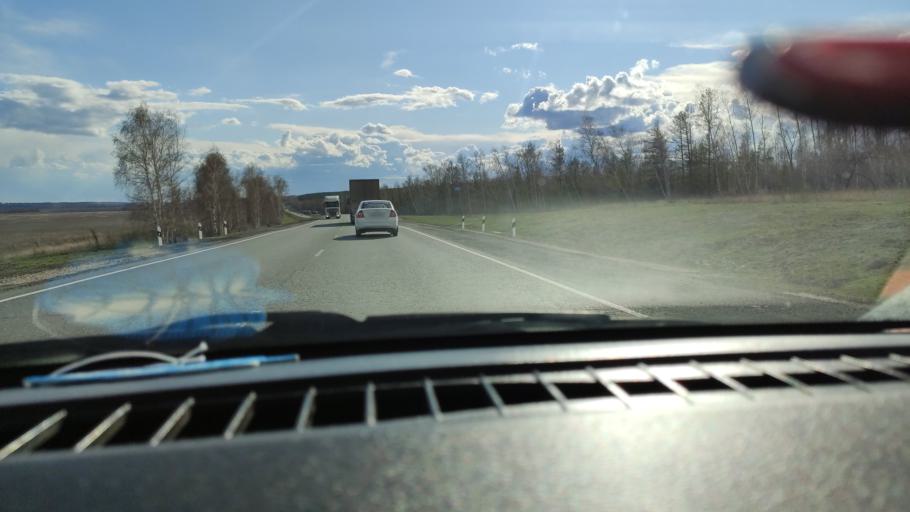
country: RU
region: Saratov
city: Sennoy
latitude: 52.1305
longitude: 46.8613
